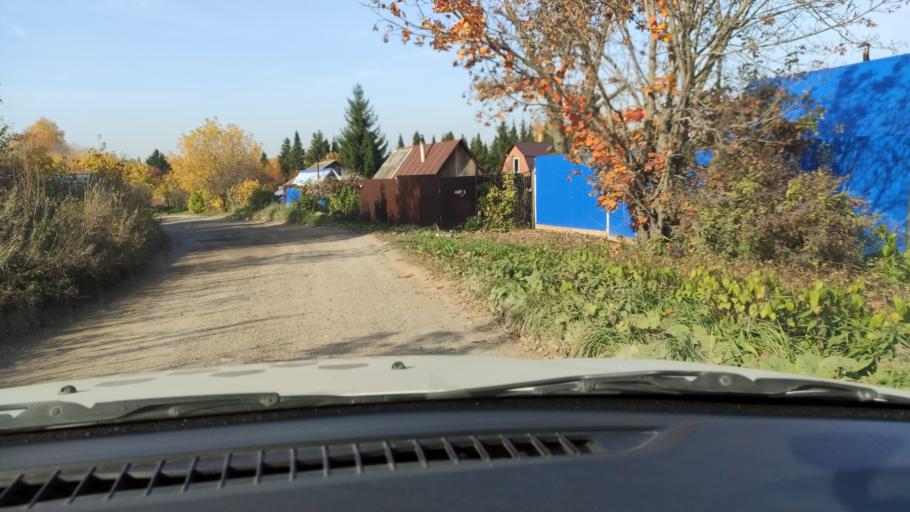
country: RU
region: Perm
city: Sylva
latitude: 58.0450
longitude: 56.7430
